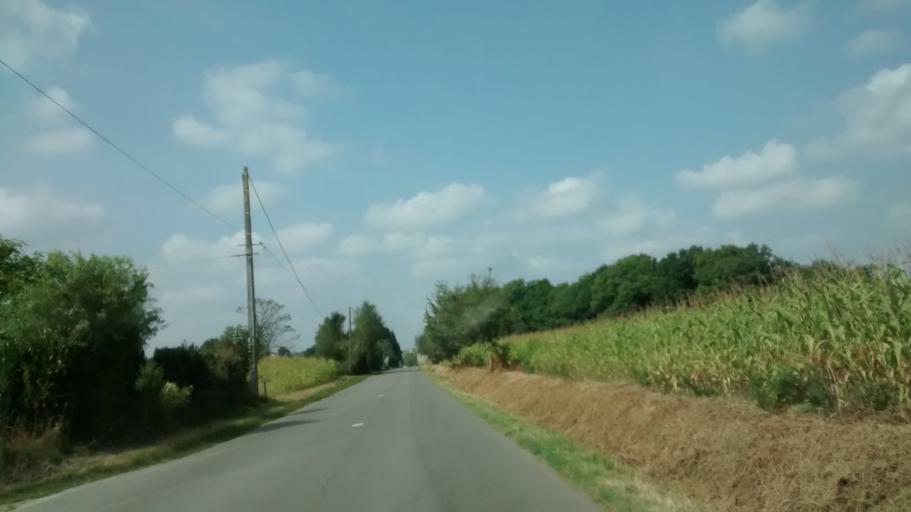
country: FR
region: Brittany
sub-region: Departement d'Ille-et-Vilaine
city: Livre-sur-Changeon
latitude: 48.2338
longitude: -1.2915
